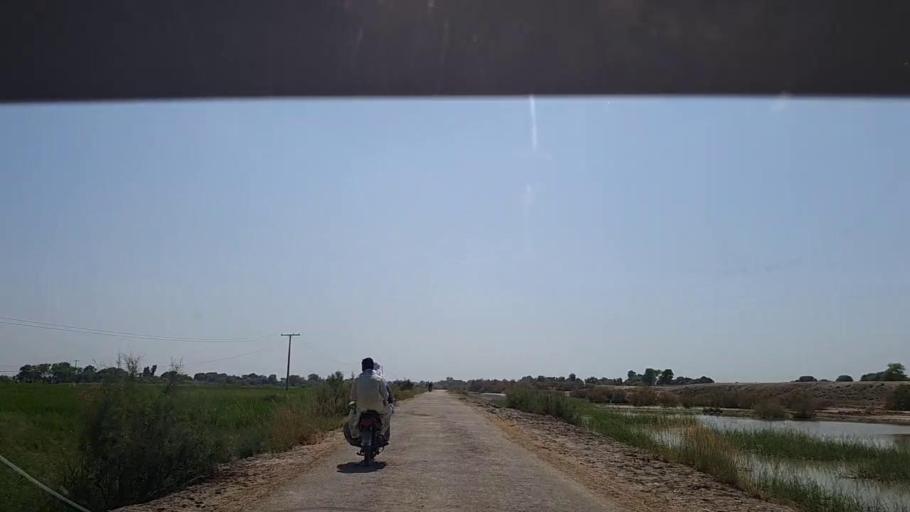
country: PK
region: Sindh
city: Kandhkot
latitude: 28.1871
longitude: 69.1613
